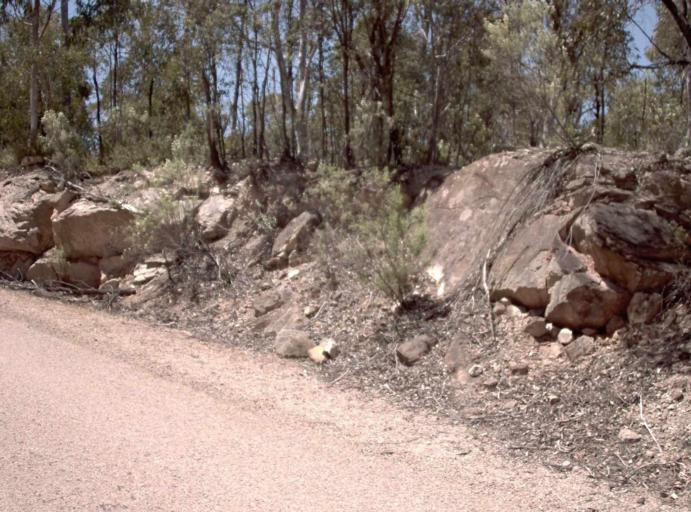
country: AU
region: New South Wales
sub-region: Snowy River
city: Jindabyne
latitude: -37.0506
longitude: 148.2752
